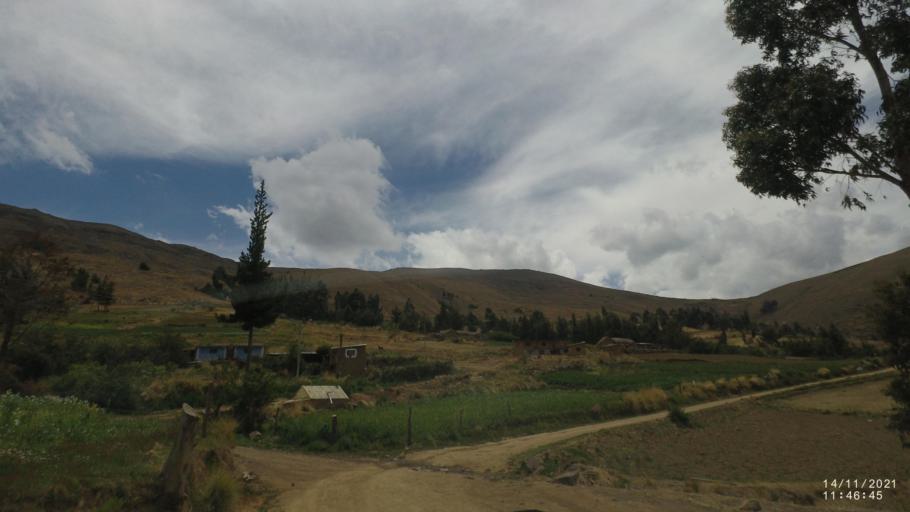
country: BO
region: Cochabamba
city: Colomi
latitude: -17.3528
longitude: -65.9866
